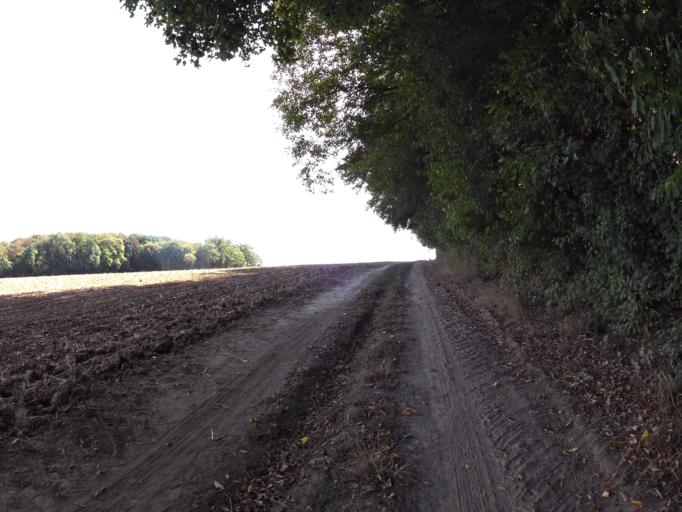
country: DE
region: Bavaria
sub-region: Regierungsbezirk Unterfranken
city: Eisingen
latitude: 49.7711
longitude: 9.8353
